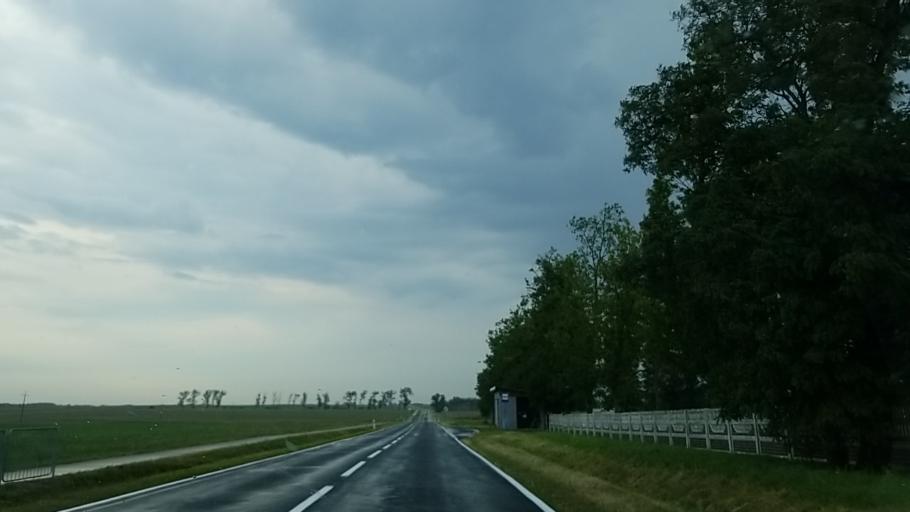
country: PL
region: Lublin Voivodeship
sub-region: Powiat wlodawski
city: Wlodawa
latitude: 51.6168
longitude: 23.5286
